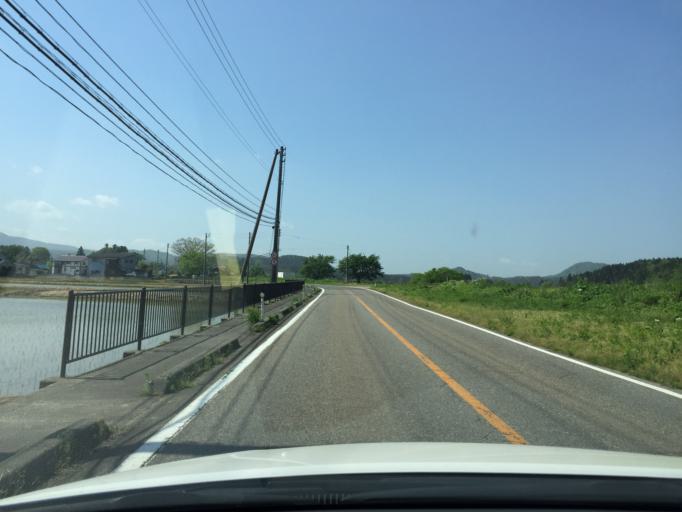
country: JP
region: Niigata
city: Muramatsu
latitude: 37.6811
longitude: 139.1500
